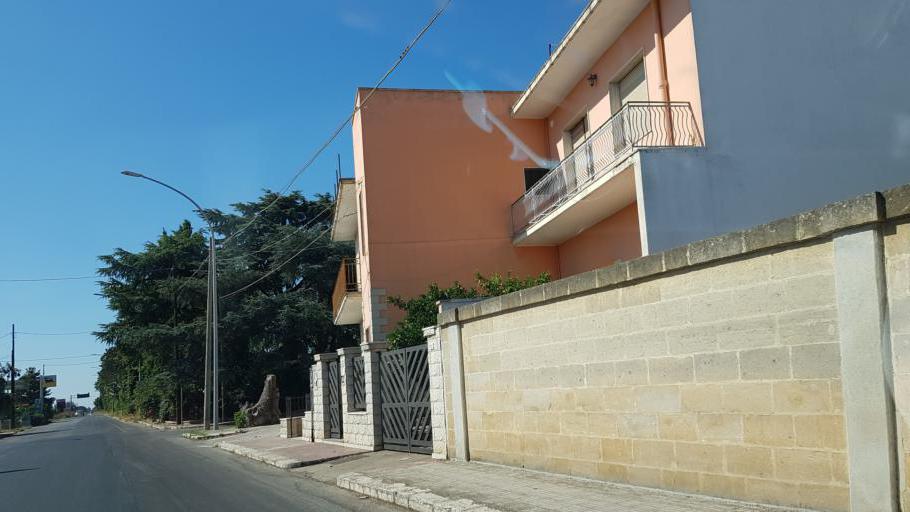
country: IT
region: Apulia
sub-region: Provincia di Brindisi
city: San Donaci
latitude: 40.4533
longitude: 17.9173
